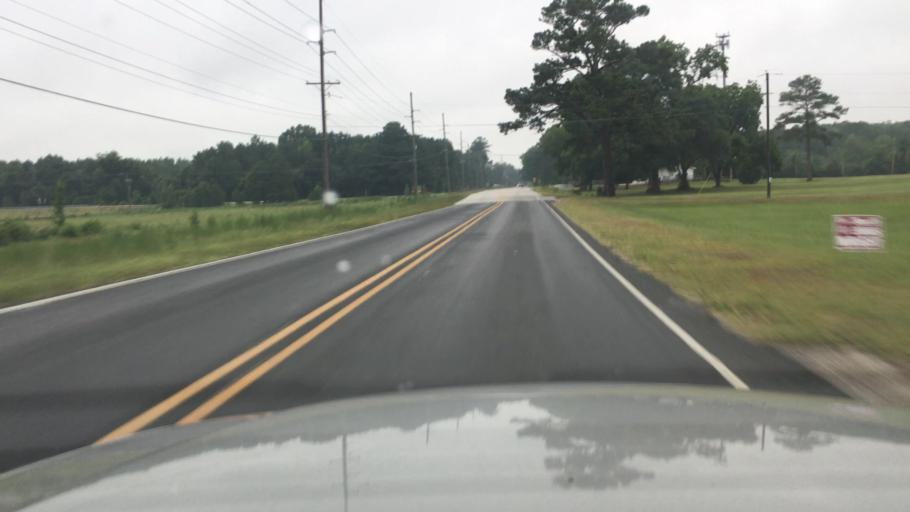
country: US
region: North Carolina
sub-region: Cumberland County
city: Fayetteville
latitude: 35.0082
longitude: -78.8632
